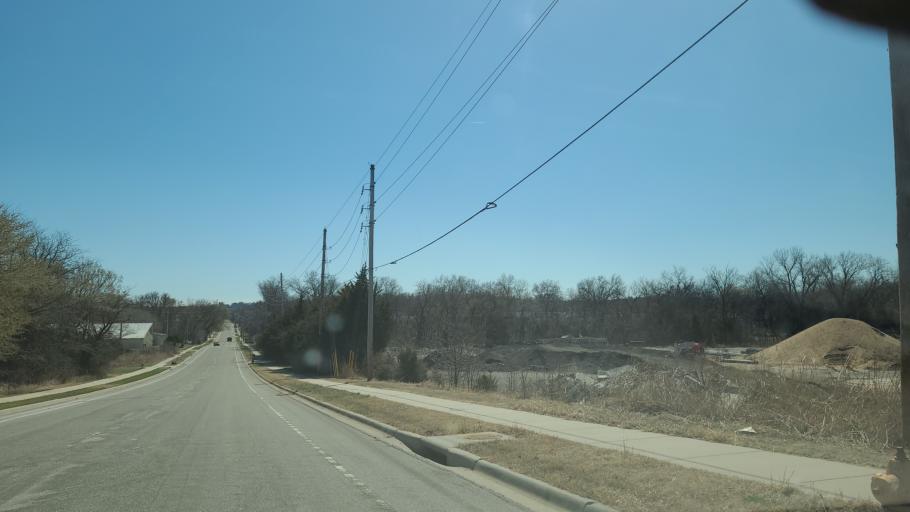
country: US
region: Kansas
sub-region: Douglas County
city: Lawrence
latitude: 38.9897
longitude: -95.2512
